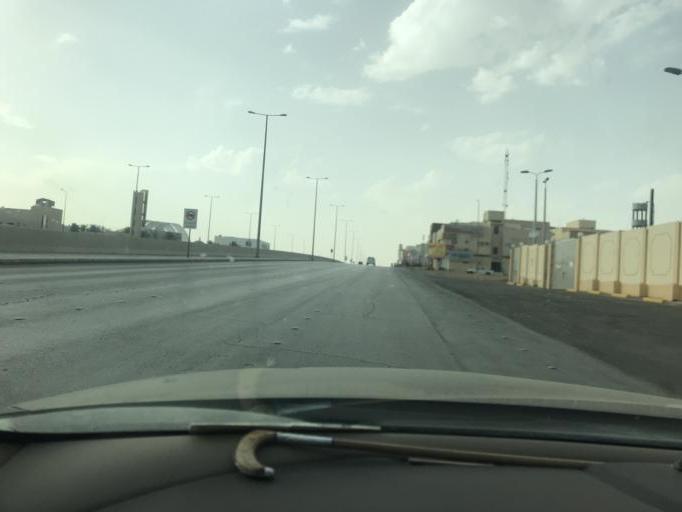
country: SA
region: Ar Riyad
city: Riyadh
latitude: 24.7779
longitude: 46.7083
